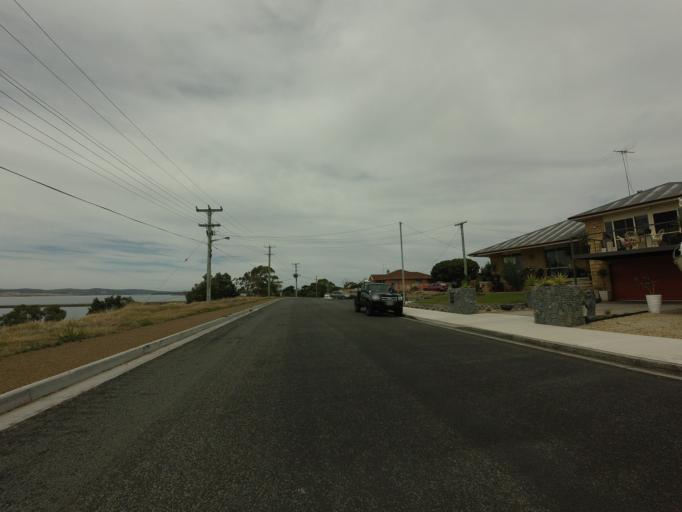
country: AU
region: Tasmania
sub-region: Sorell
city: Sorell
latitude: -42.7965
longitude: 147.5362
